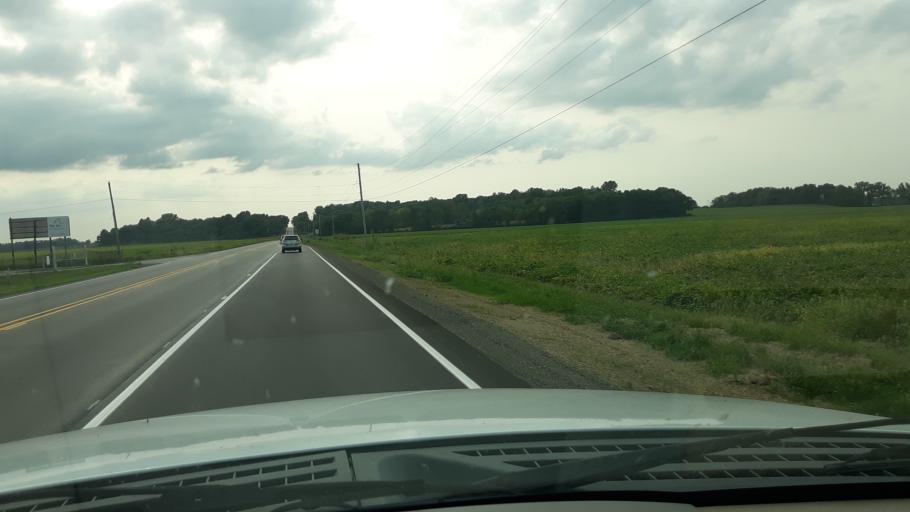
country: US
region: Indiana
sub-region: Gibson County
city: Princeton
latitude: 38.3558
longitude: -87.6435
